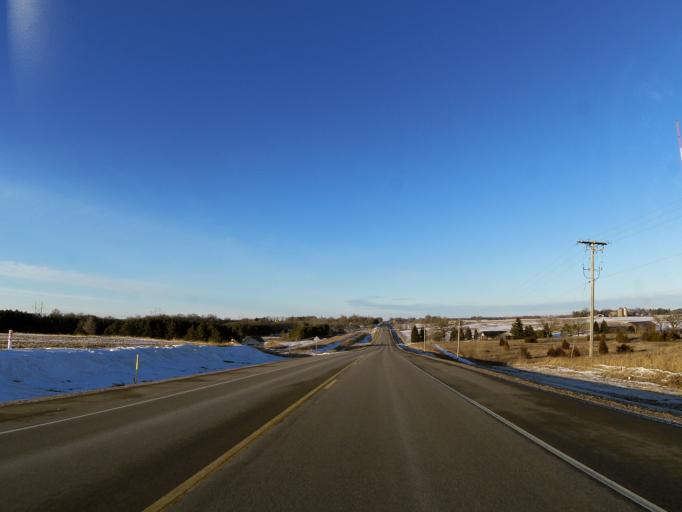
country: US
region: Minnesota
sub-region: Washington County
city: Cottage Grove
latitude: 44.8668
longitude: -92.9032
